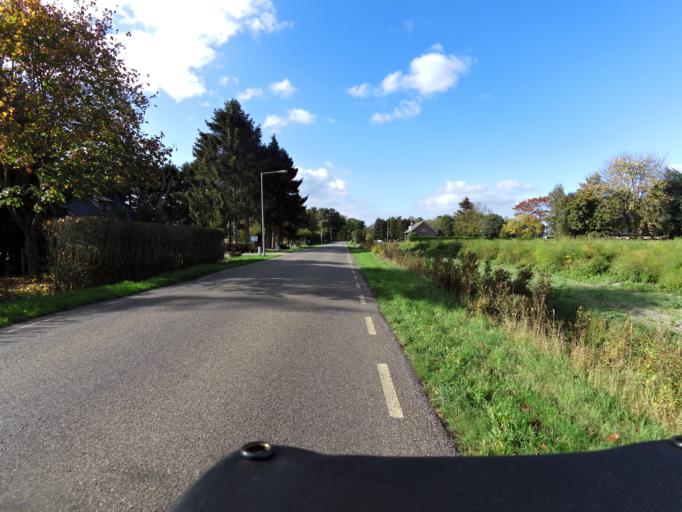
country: NL
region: North Brabant
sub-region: Gemeente Bergen op Zoom
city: Lepelstraat
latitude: 51.5482
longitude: 4.2862
